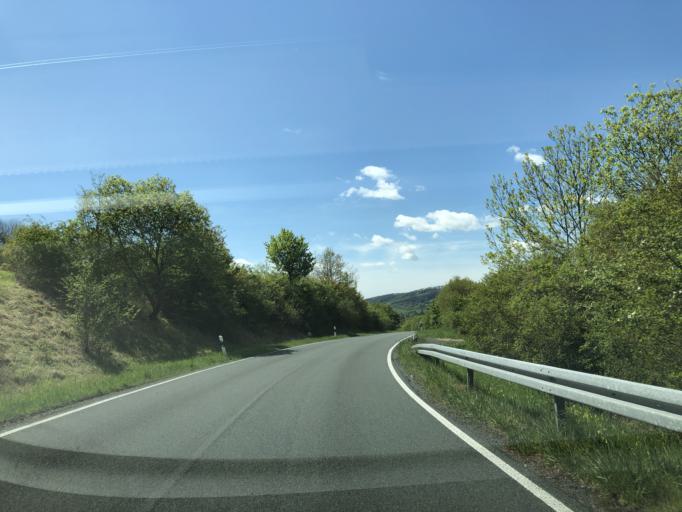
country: DE
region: Hesse
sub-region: Regierungsbezirk Kassel
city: Grossalmerode
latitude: 51.2421
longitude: 9.8378
